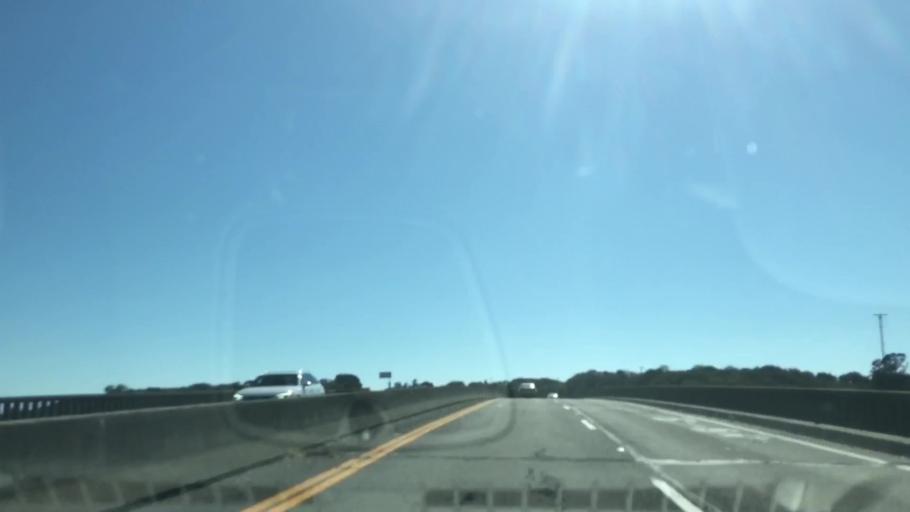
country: US
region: California
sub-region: Marin County
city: Black Point-Green Point
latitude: 38.1161
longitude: -122.5049
